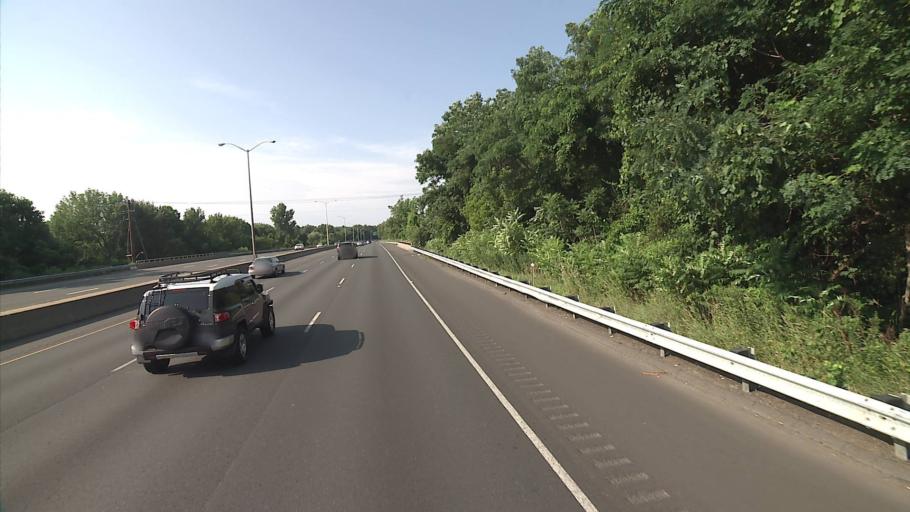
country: US
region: Connecticut
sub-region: Hartford County
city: Enfield
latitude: 41.9643
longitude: -72.5904
